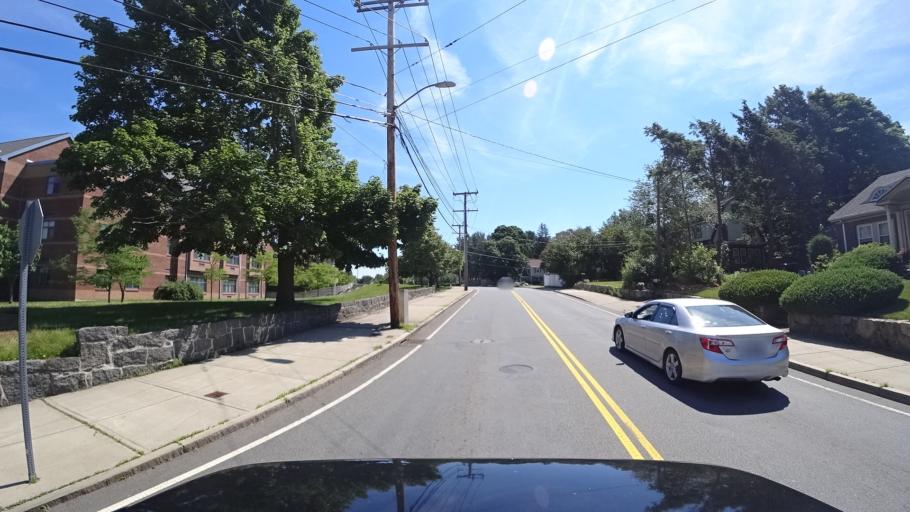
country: US
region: Massachusetts
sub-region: Norfolk County
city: Dedham
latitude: 42.2437
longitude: -71.1675
